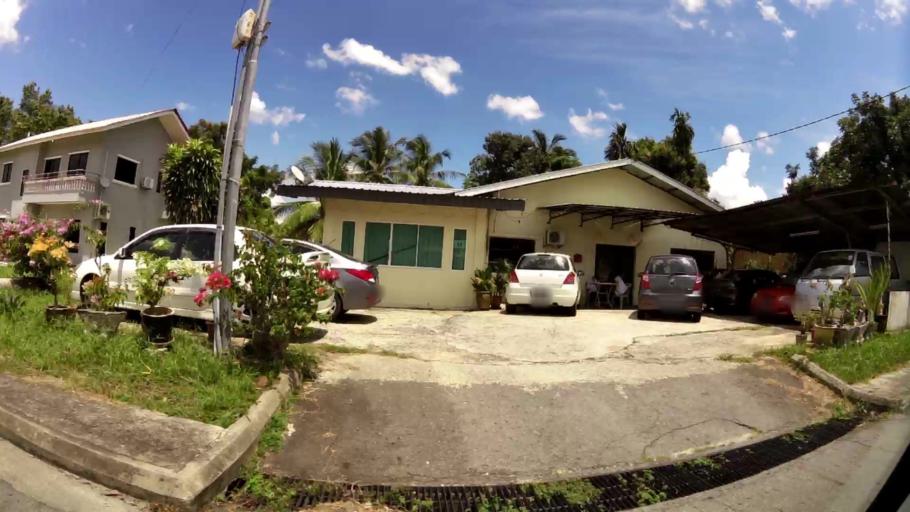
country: BN
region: Brunei and Muara
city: Bandar Seri Begawan
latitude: 4.9462
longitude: 114.9646
